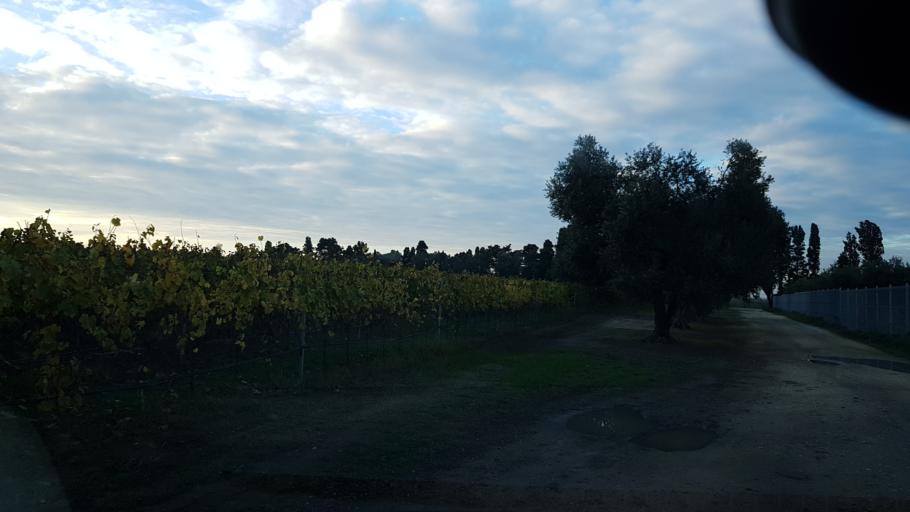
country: IT
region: Apulia
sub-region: Provincia di Brindisi
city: La Rosa
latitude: 40.5938
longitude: 17.9844
